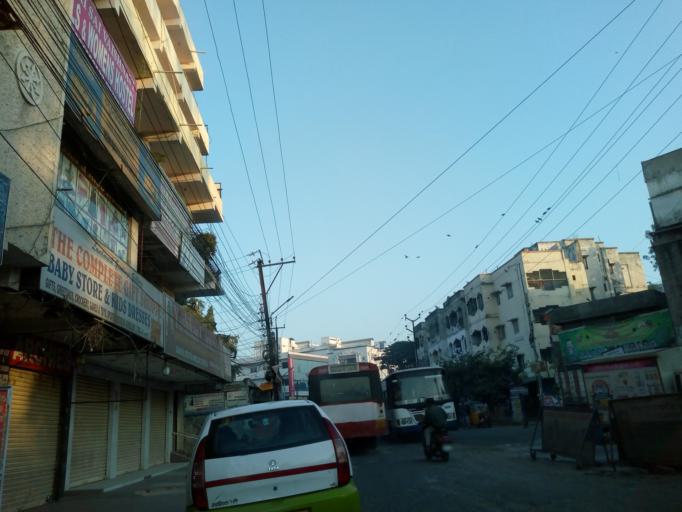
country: IN
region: Telangana
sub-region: Rangareddi
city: Gaddi Annaram
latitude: 17.4034
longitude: 78.5104
